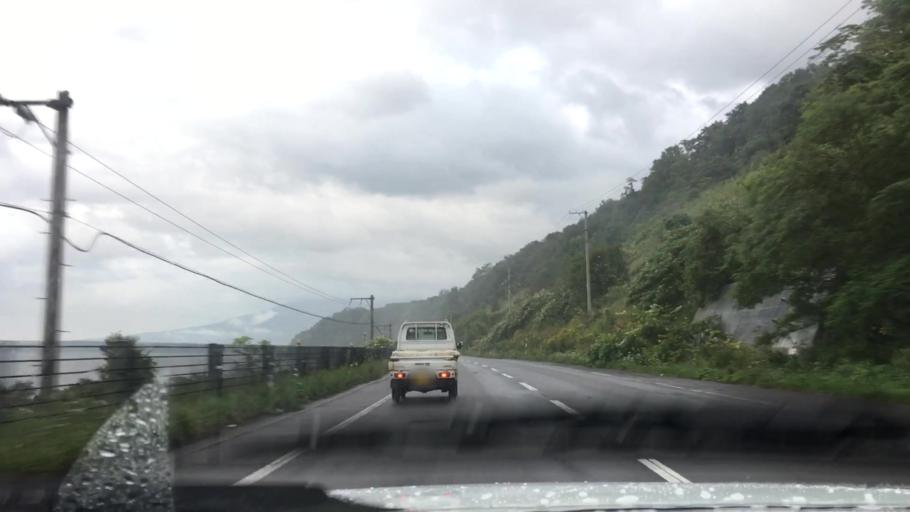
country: JP
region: Hokkaido
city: Nanae
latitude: 42.1253
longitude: 140.5203
